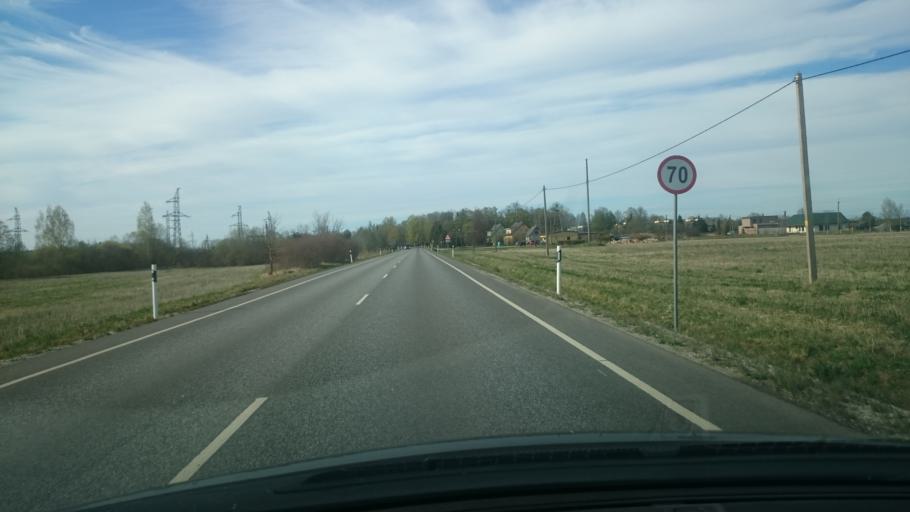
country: EE
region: Ida-Virumaa
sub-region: Johvi vald
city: Johvi
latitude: 59.2666
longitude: 27.5140
